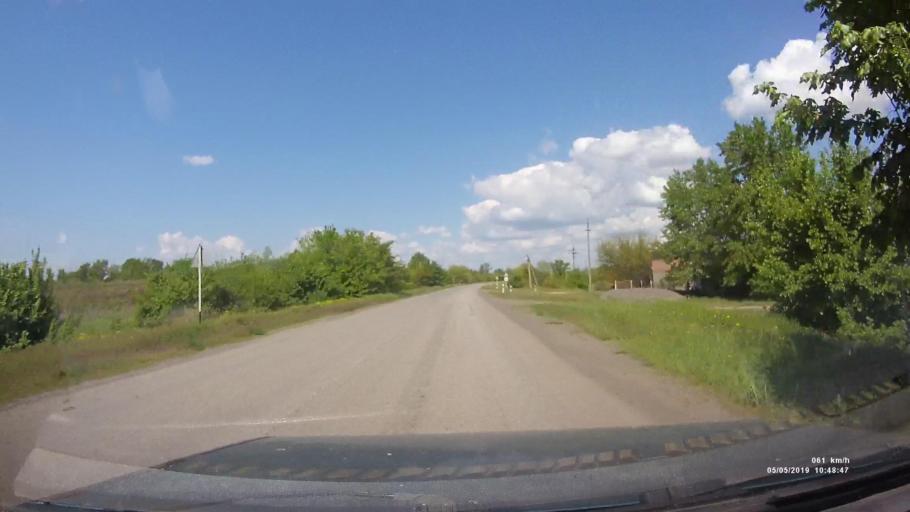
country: RU
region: Rostov
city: Ust'-Donetskiy
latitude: 47.6442
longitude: 40.8158
